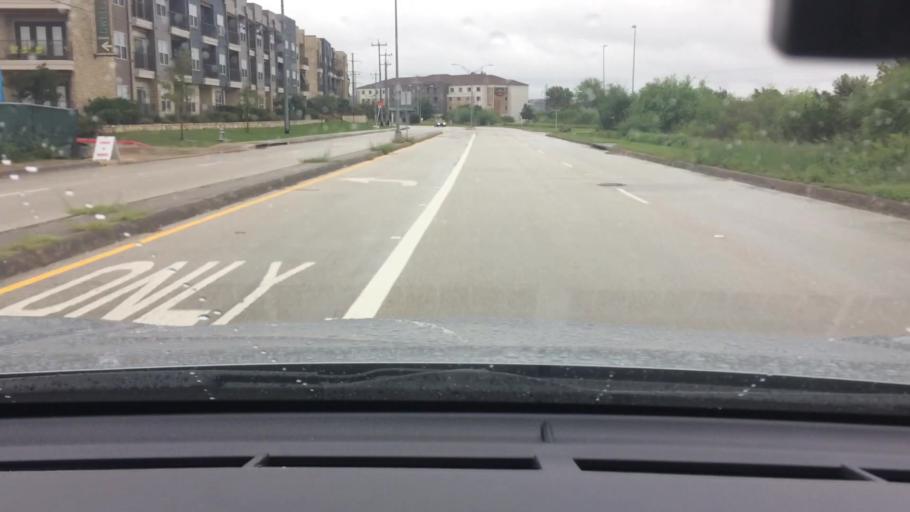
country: US
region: Texas
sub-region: Bexar County
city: Hollywood Park
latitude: 29.6117
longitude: -98.4623
